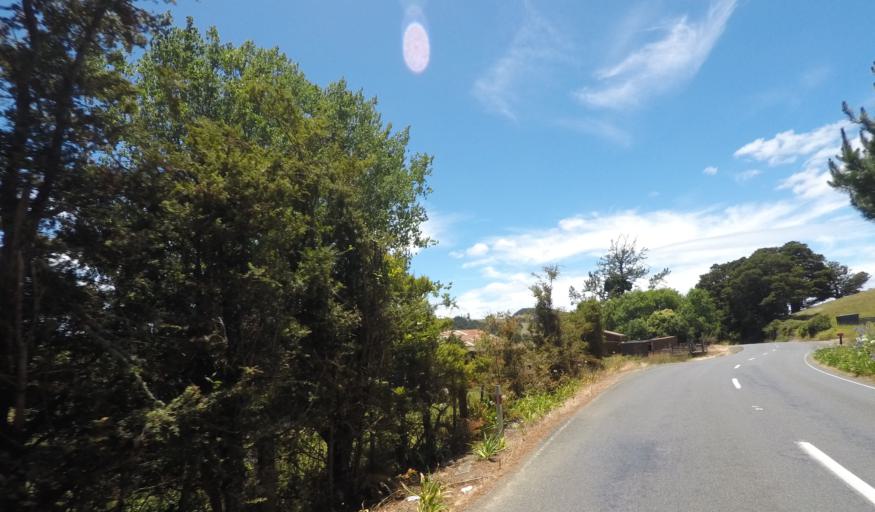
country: NZ
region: Northland
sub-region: Whangarei
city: Whangarei
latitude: -35.5361
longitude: 174.3132
